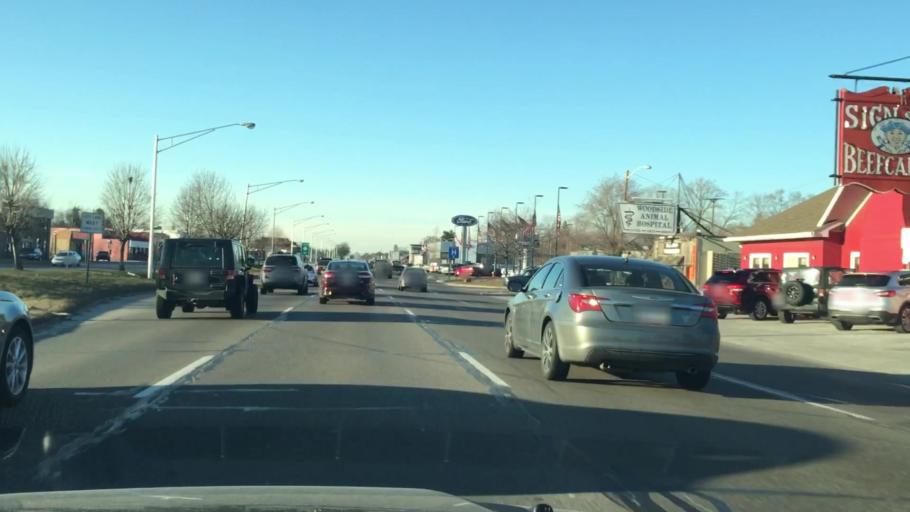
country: US
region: Michigan
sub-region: Oakland County
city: Huntington Woods
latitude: 42.4919
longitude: -83.1604
